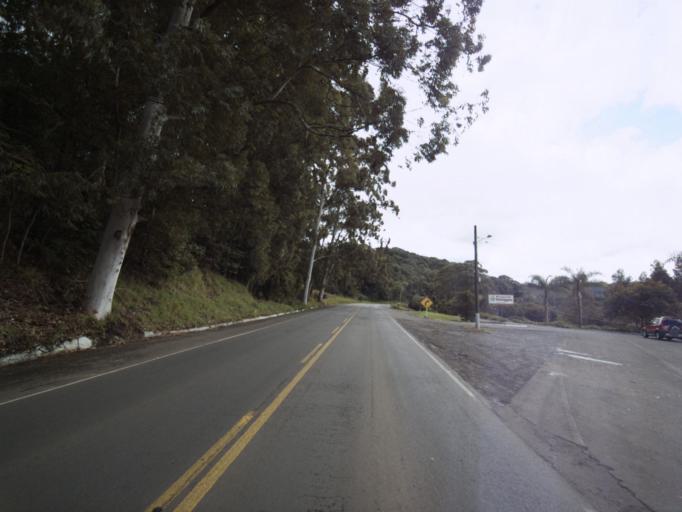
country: BR
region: Santa Catarina
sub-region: Concordia
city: Concordia
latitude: -27.2095
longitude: -51.9516
